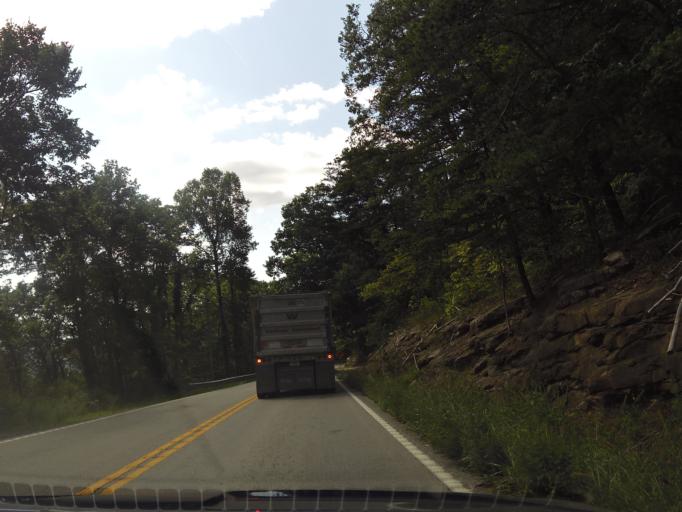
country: US
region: Kentucky
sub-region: Harlan County
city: Harlan
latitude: 36.8819
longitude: -83.3088
